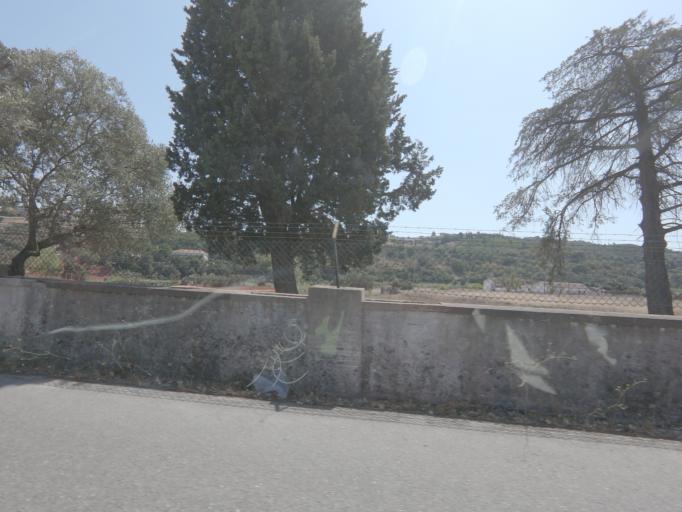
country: PT
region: Setubal
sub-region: Setubal
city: Setubal
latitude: 38.5325
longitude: -8.9115
